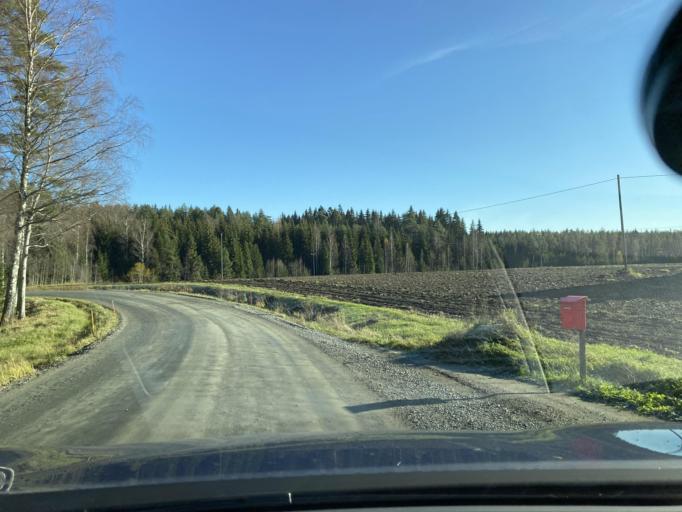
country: FI
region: Haeme
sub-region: Haemeenlinna
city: Kalvola
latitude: 61.0056
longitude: 24.1195
